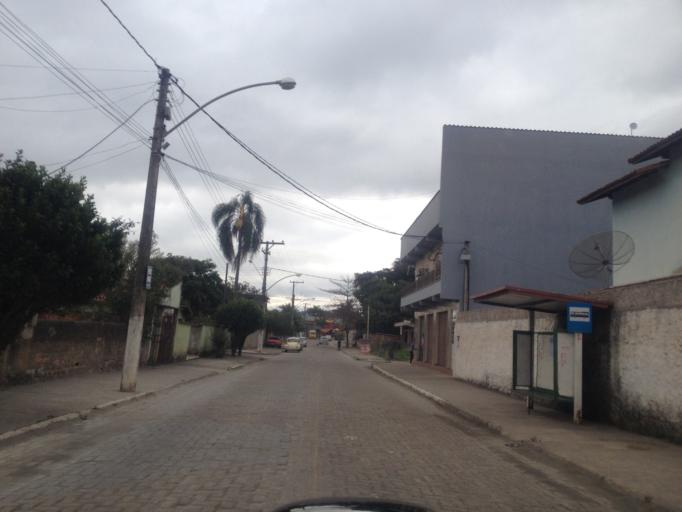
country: BR
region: Rio de Janeiro
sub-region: Porto Real
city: Porto Real
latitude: -22.4120
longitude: -44.2962
